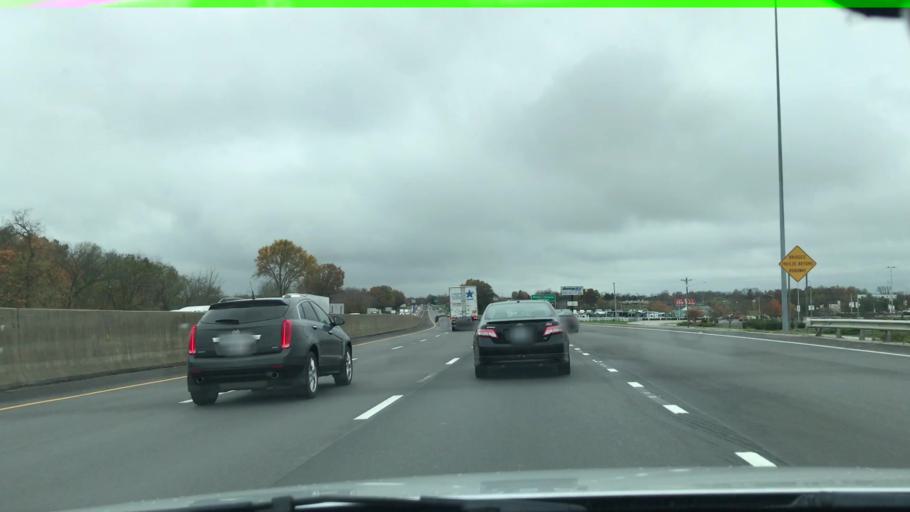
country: US
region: Kentucky
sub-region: Warren County
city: Bowling Green
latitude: 37.0045
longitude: -86.3711
